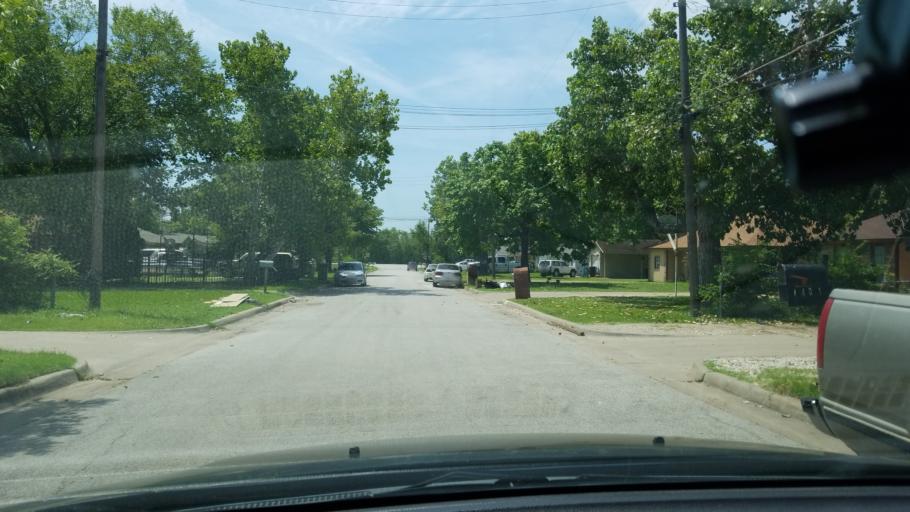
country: US
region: Texas
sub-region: Dallas County
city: Balch Springs
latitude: 32.7501
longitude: -96.6281
